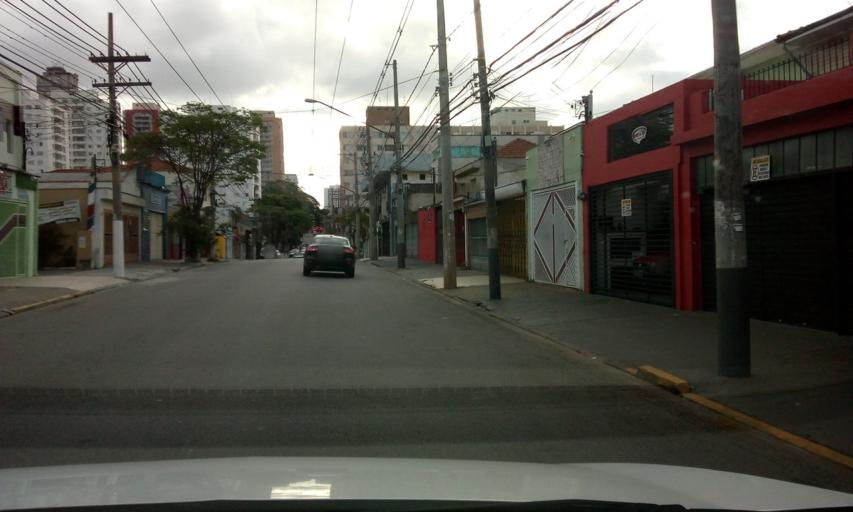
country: BR
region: Sao Paulo
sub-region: Sao Paulo
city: Sao Paulo
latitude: -23.5443
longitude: -46.5597
